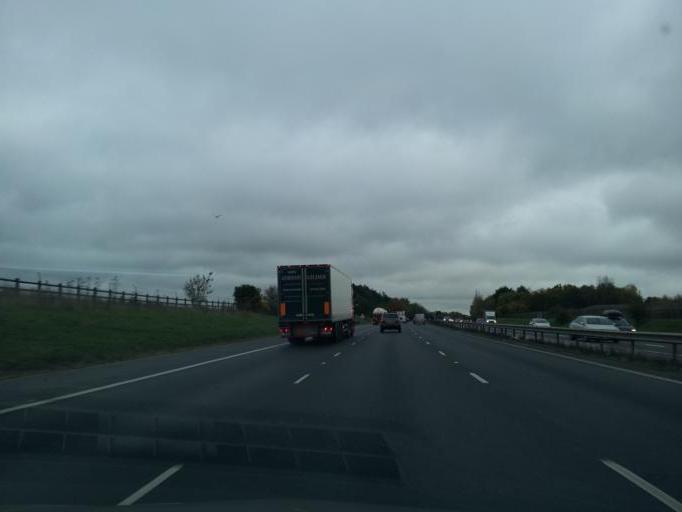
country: GB
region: England
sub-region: Oxfordshire
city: Bicester
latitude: 51.8862
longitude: -1.2048
